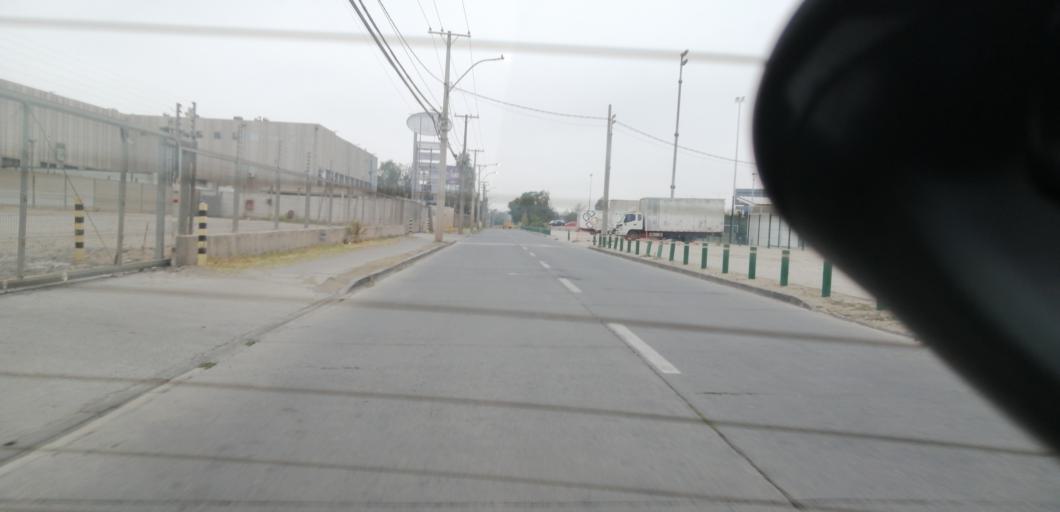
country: CL
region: Santiago Metropolitan
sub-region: Provincia de Santiago
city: Lo Prado
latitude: -33.4482
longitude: -70.7708
